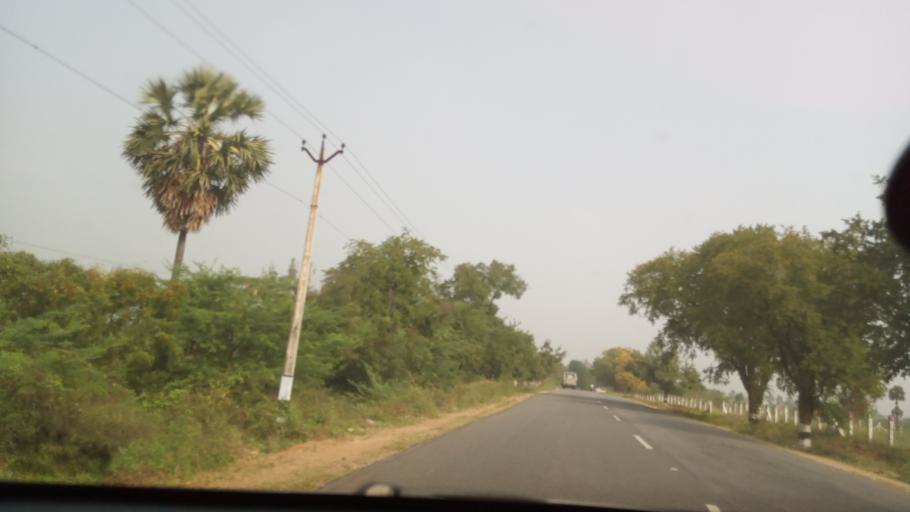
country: IN
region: Tamil Nadu
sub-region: Erode
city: Punjai Puliyampatti
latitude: 11.4098
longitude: 77.1929
